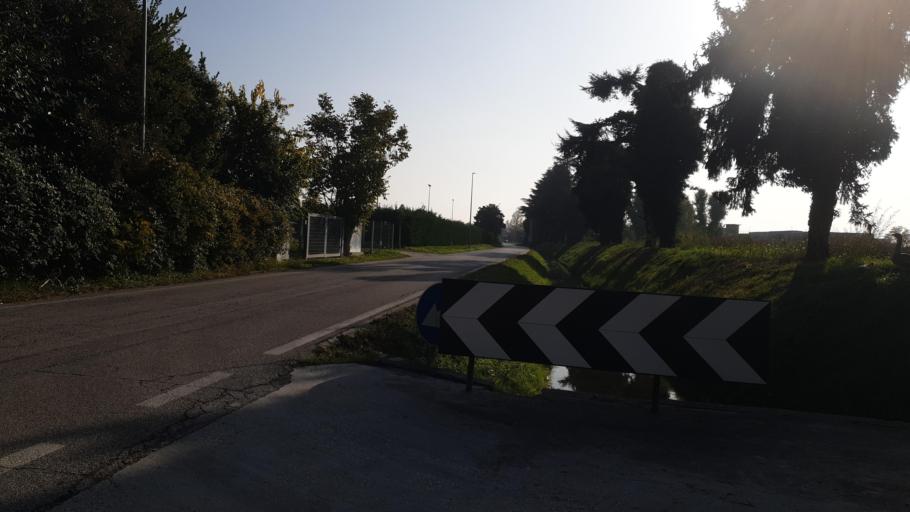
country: IT
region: Veneto
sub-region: Provincia di Padova
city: Oltre Brenta
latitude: 45.4021
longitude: 11.9974
